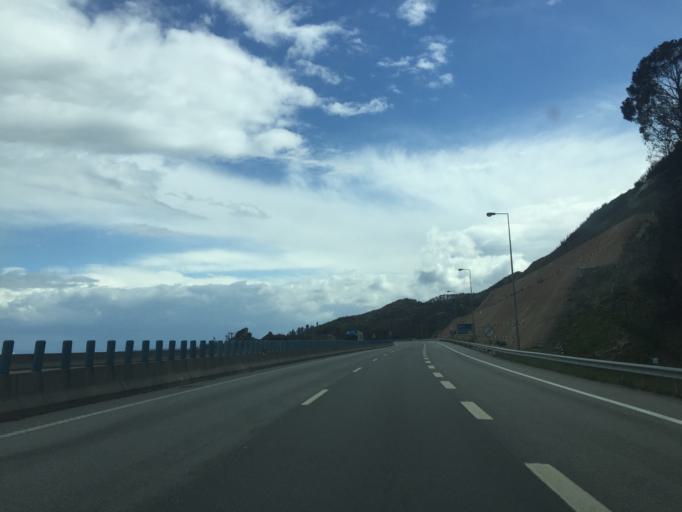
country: PT
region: Viseu
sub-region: Vouzela
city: Vouzela
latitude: 40.6916
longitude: -8.0787
